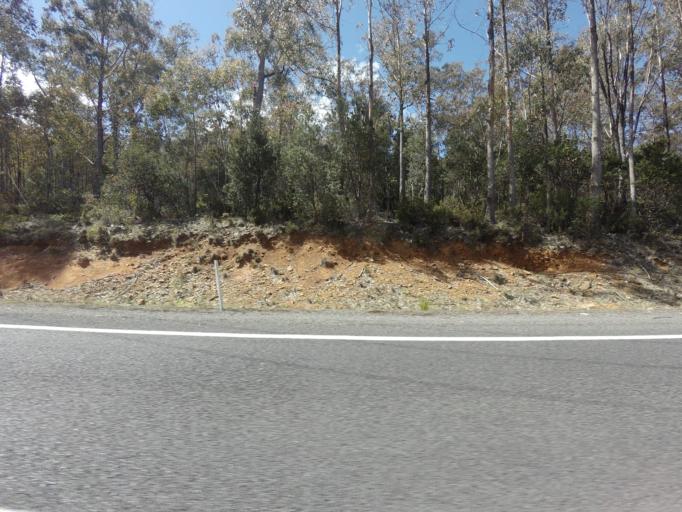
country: AU
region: Tasmania
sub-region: Northern Midlands
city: Evandale
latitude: -42.0328
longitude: 147.8109
